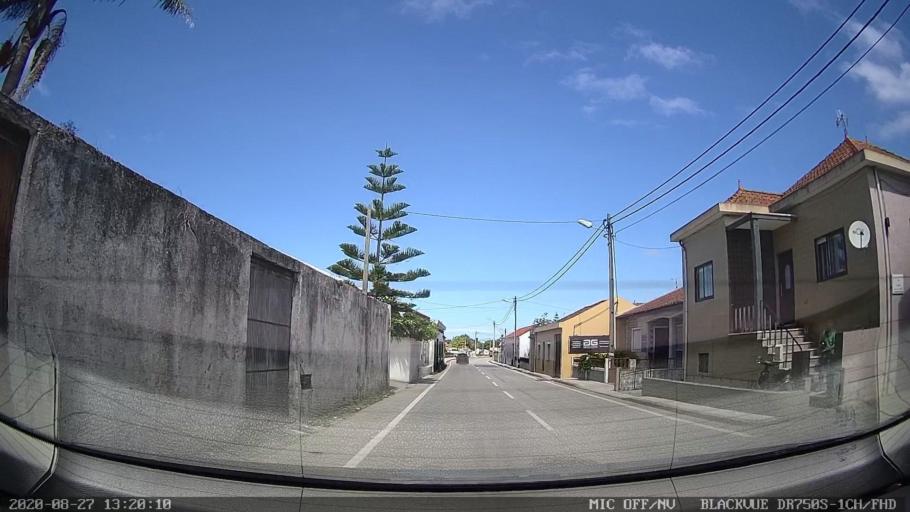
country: PT
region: Aveiro
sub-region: Vagos
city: Vagos
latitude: 40.5585
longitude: -8.6823
